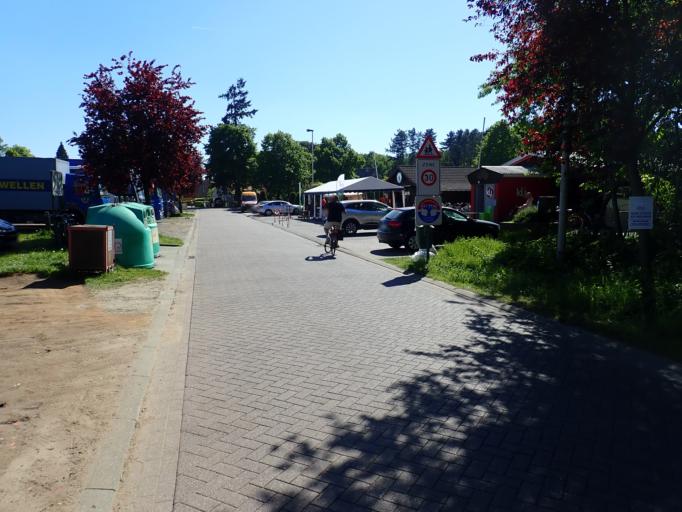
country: BE
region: Flanders
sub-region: Provincie Antwerpen
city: Zandhoven
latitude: 51.2187
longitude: 4.6621
